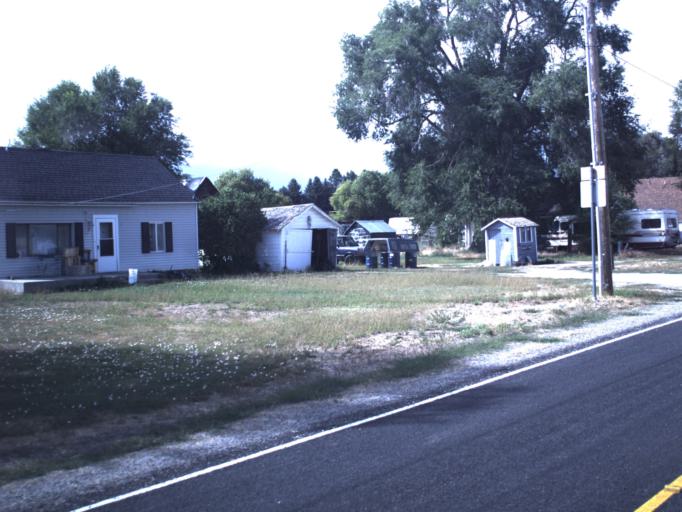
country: US
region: Utah
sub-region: Cache County
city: Benson
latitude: 41.9185
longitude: -112.0451
